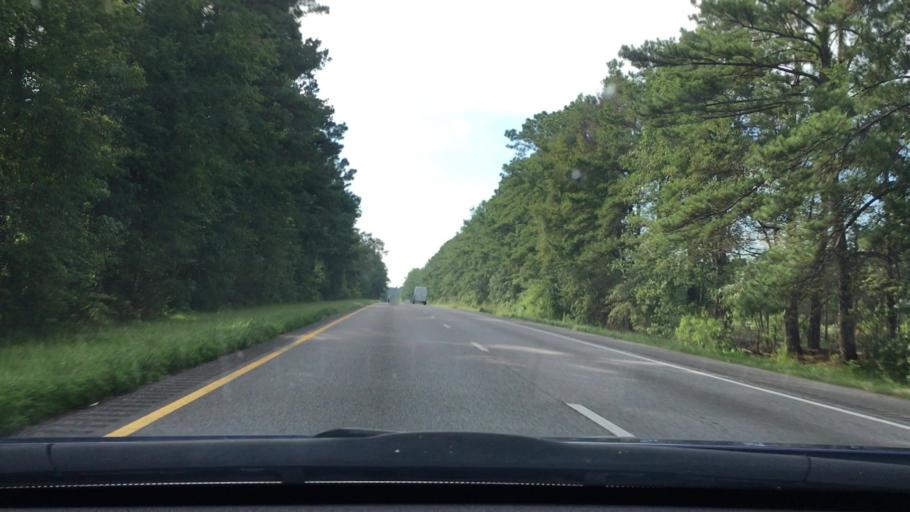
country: US
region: South Carolina
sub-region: Dorchester County
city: Ridgeville
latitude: 33.1602
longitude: -80.3534
